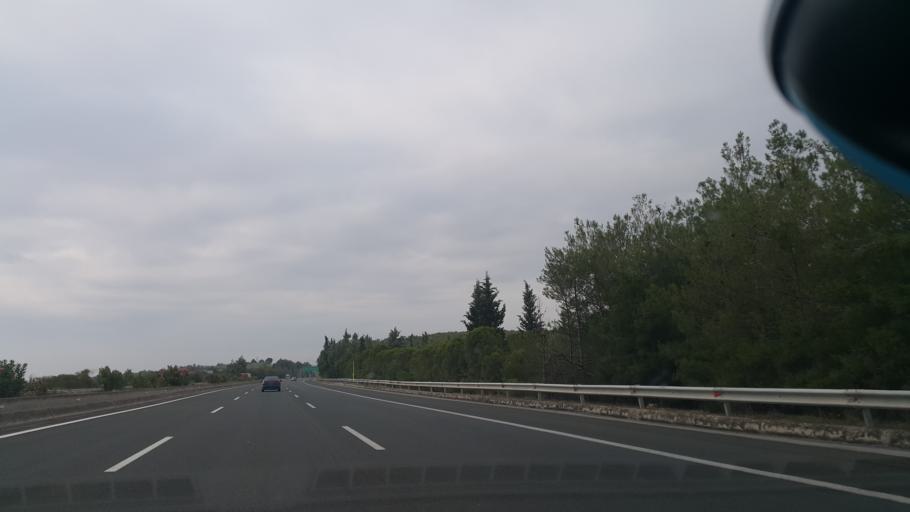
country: GR
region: Central Macedonia
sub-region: Nomos Pierias
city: Makrygialos
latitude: 40.4314
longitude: 22.5877
